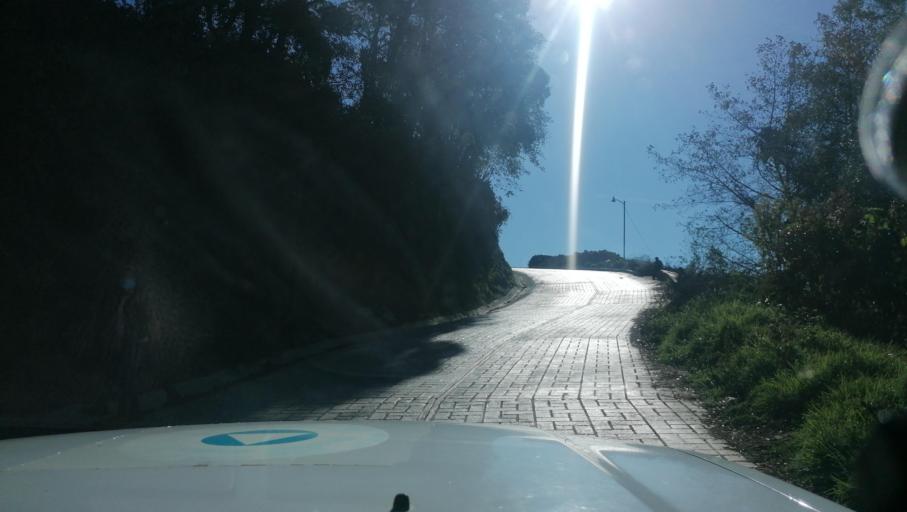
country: MX
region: Chiapas
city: Motozintla de Mendoza
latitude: 15.2559
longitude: -92.2137
